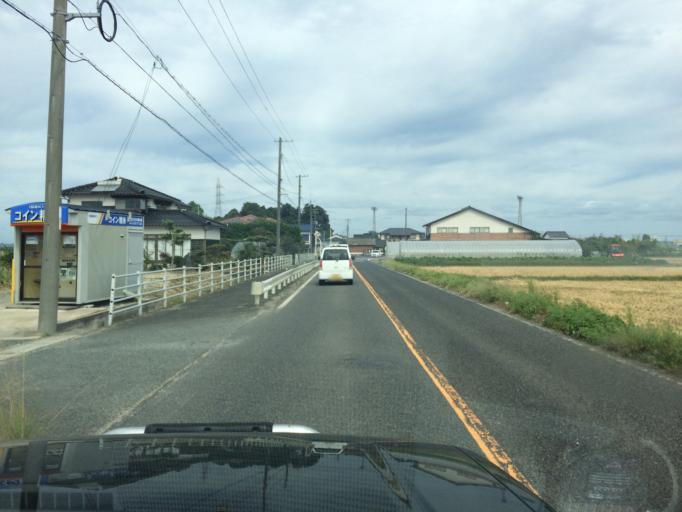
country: JP
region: Tottori
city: Tottori
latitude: 35.5065
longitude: 134.1930
